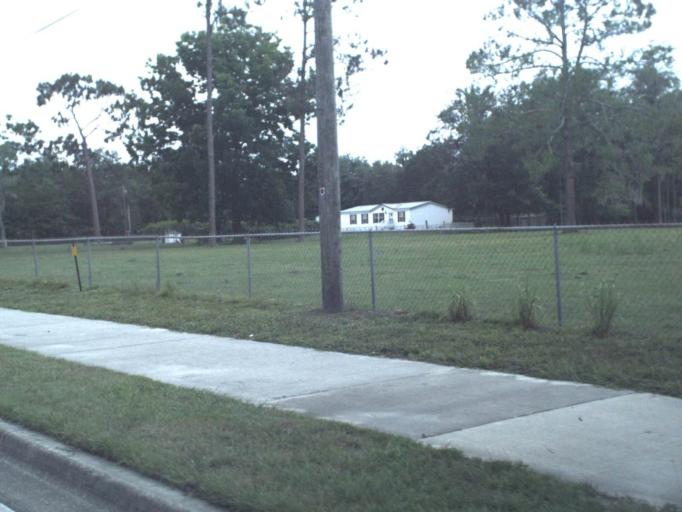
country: US
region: Florida
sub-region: Columbia County
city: Five Points
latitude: 30.2281
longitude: -82.6386
